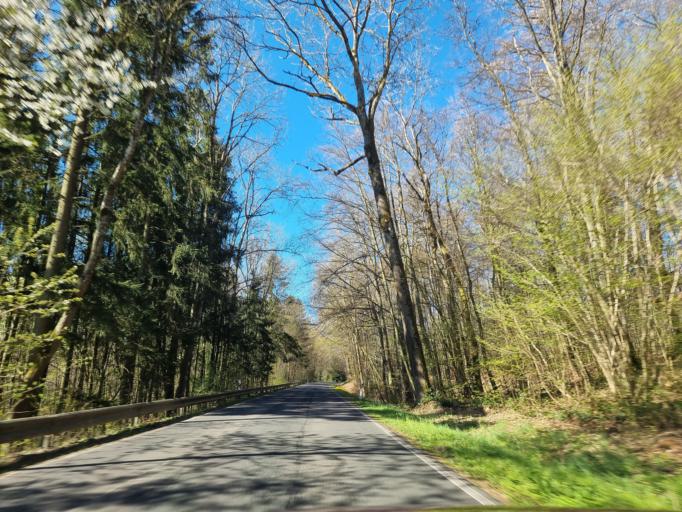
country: DE
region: Rheinland-Pfalz
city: Dahlem
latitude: 49.8976
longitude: 6.5950
